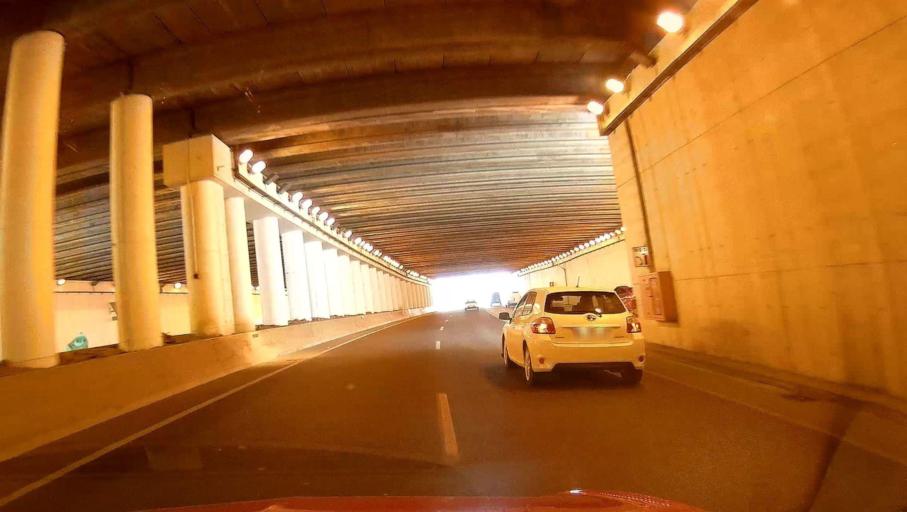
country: ES
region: Balearic Islands
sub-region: Illes Balears
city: Ibiza
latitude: 38.8965
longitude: 1.4012
